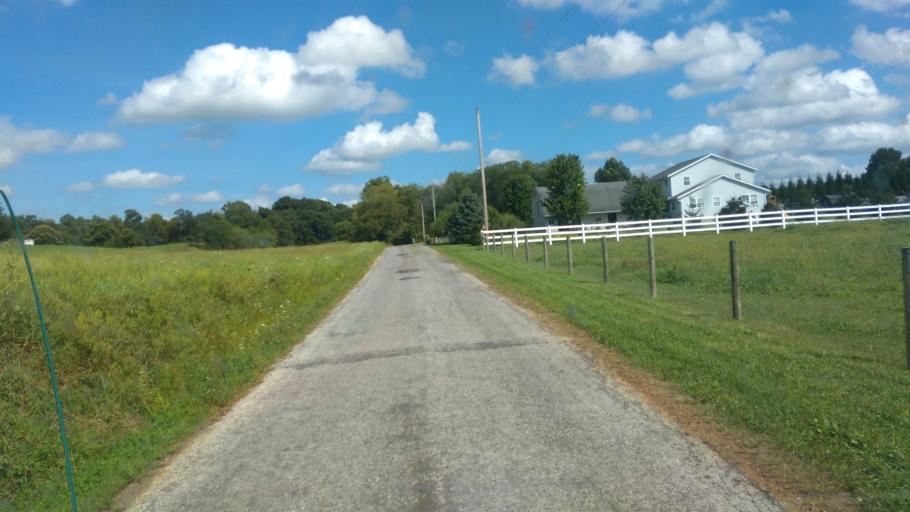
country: US
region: Ohio
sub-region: Holmes County
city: Millersburg
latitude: 40.6489
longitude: -81.9047
